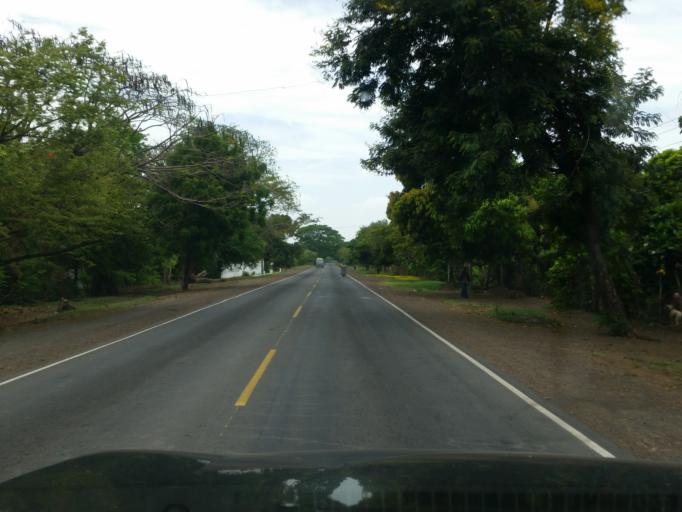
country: NI
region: Granada
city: Diriomo
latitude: 11.8232
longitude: -86.0388
